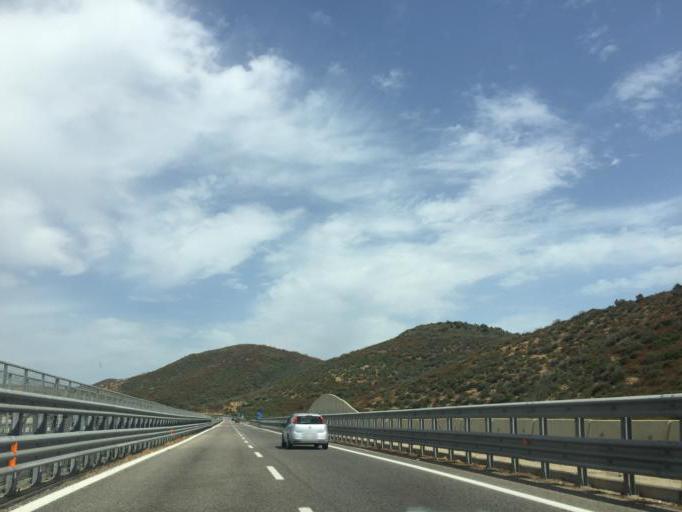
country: IT
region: Sardinia
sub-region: Provincia di Olbia-Tempio
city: San Teodoro
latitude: 40.7665
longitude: 9.6411
